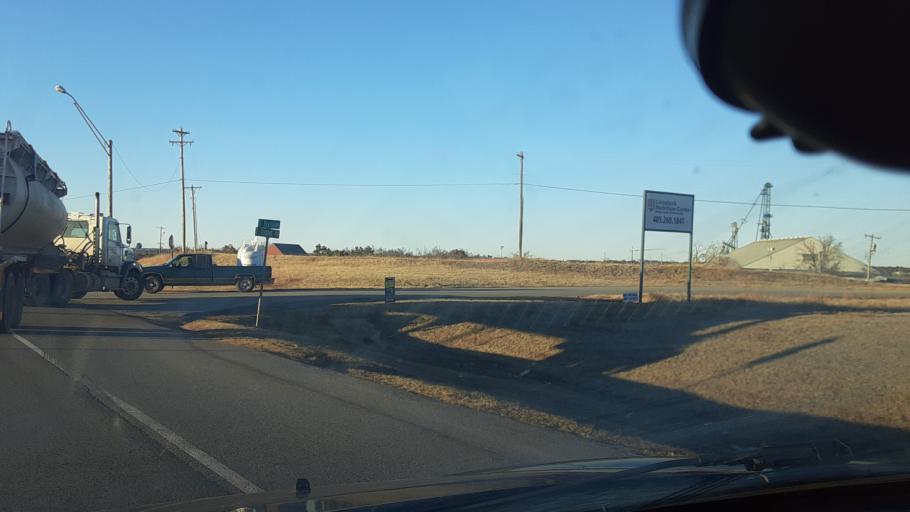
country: US
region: Oklahoma
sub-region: Logan County
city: Guthrie
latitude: 35.8264
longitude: -97.4224
